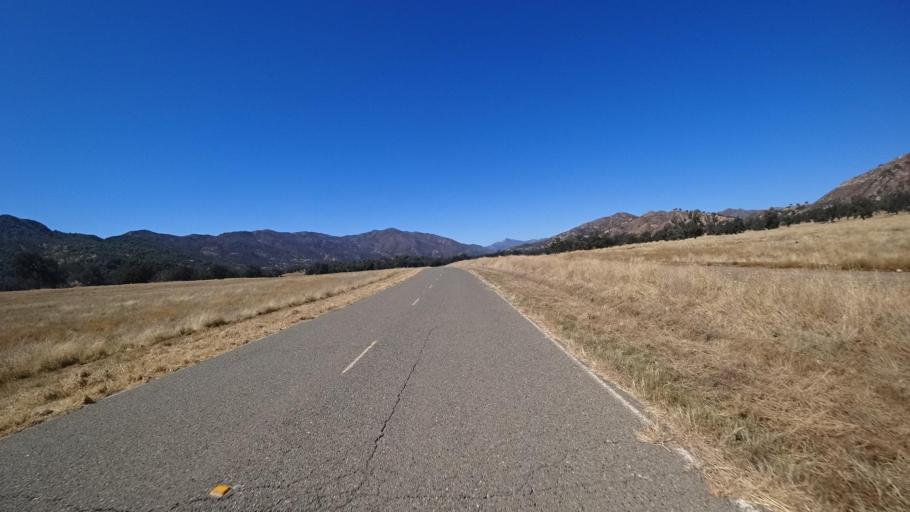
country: US
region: California
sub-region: Monterey County
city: King City
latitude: 35.9678
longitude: -121.3146
